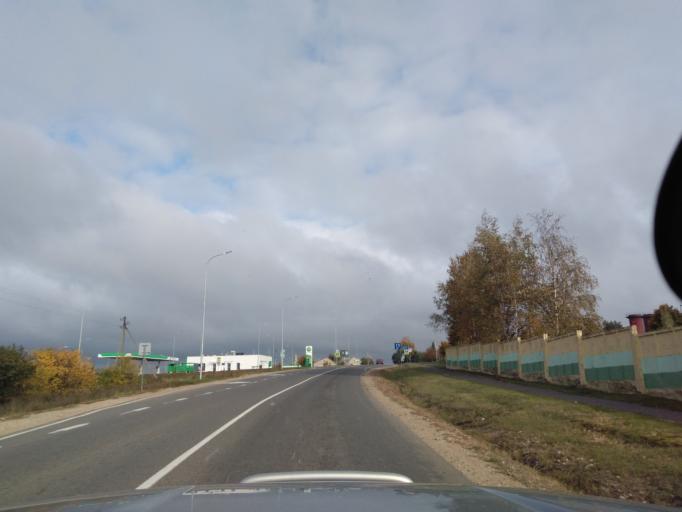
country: BY
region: Minsk
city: Kapyl'
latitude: 53.1476
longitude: 27.0751
